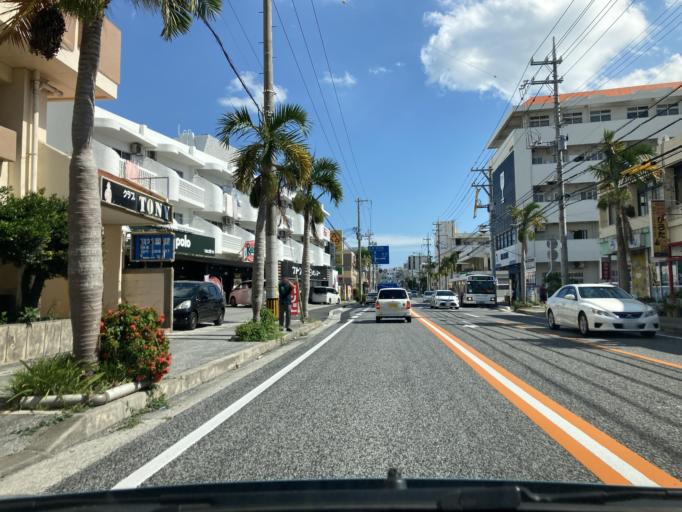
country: JP
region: Okinawa
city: Ginowan
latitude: 26.2625
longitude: 127.7411
